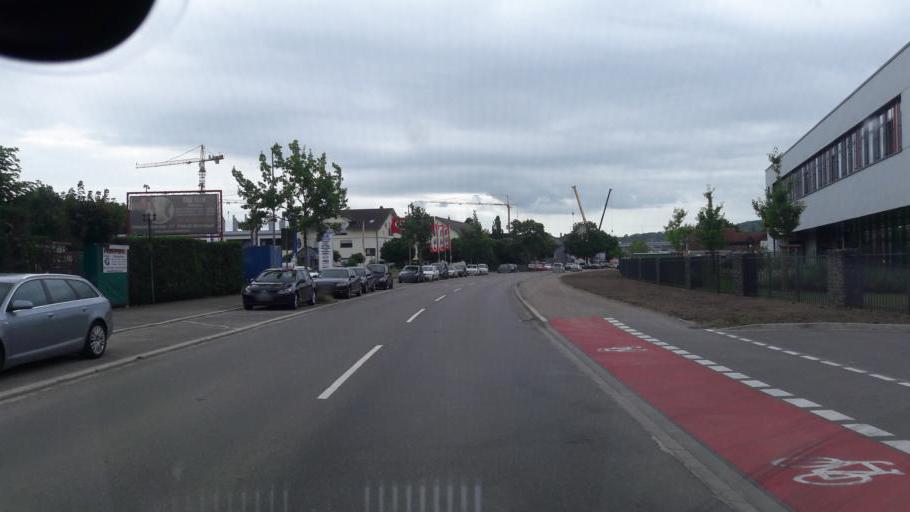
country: DE
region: Baden-Wuerttemberg
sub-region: Karlsruhe Region
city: Bruchsal
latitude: 49.1270
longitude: 8.5711
